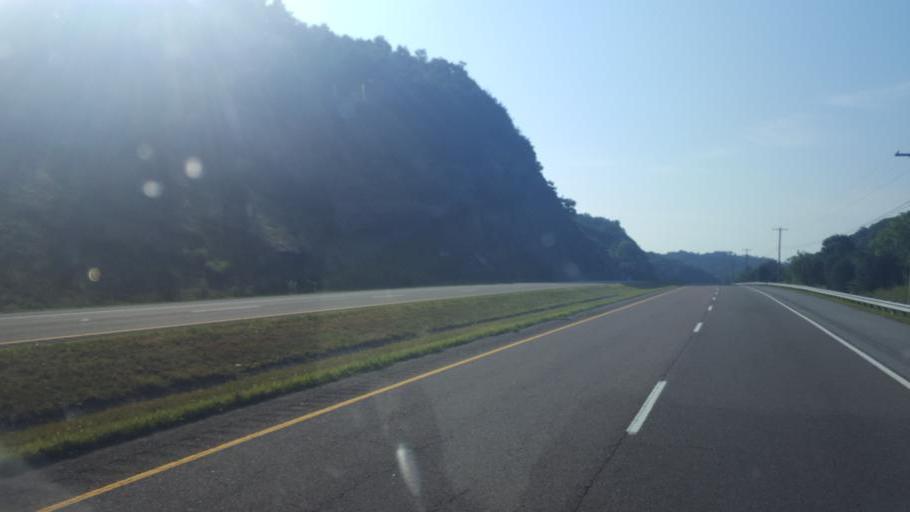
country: US
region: Tennessee
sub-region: Carter County
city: Elizabethton
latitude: 36.4045
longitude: -82.2371
